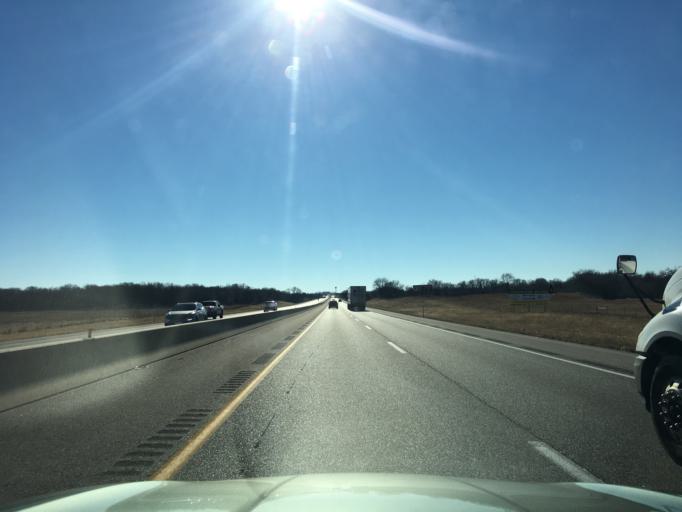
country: US
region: Kansas
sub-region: Sumner County
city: Belle Plaine
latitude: 37.3898
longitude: -97.3253
